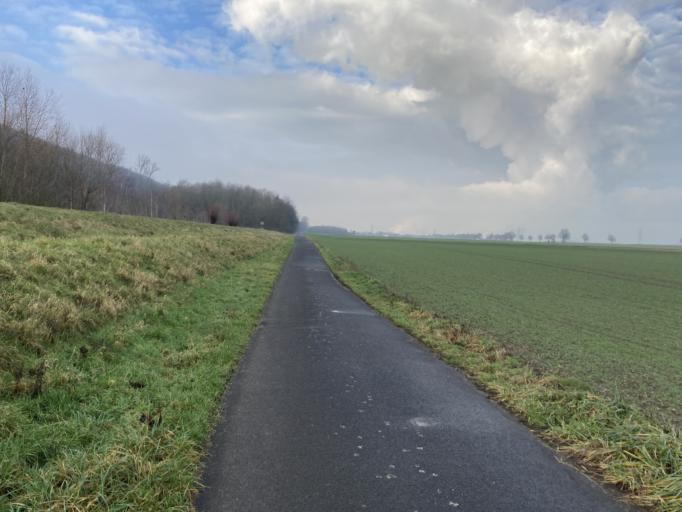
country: DE
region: North Rhine-Westphalia
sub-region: Regierungsbezirk Koln
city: Bergheim
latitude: 50.9598
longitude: 6.7212
